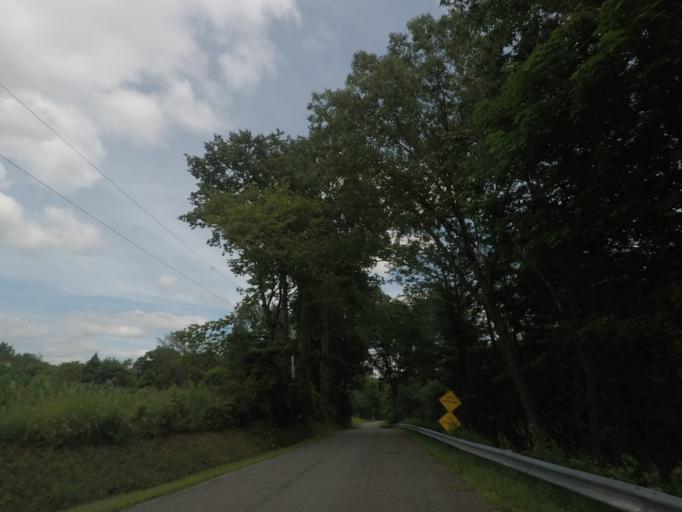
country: US
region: New York
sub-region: Saratoga County
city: Stillwater
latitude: 43.0093
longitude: -73.6253
